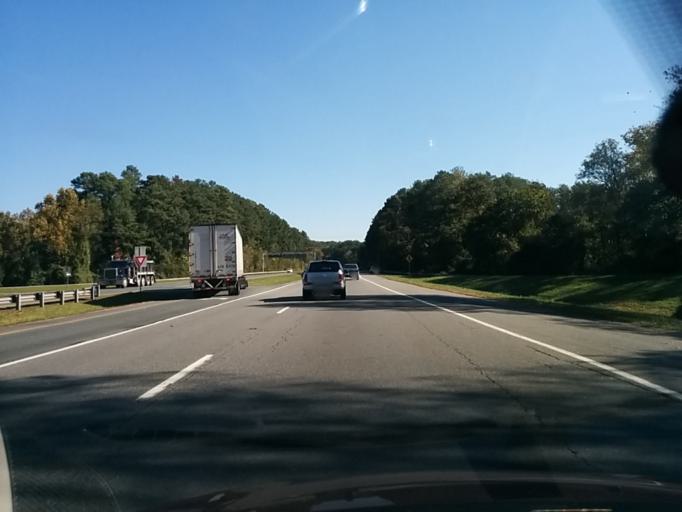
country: US
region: Virginia
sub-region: City of Charlottesville
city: Charlottesville
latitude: 38.0211
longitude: -78.5359
